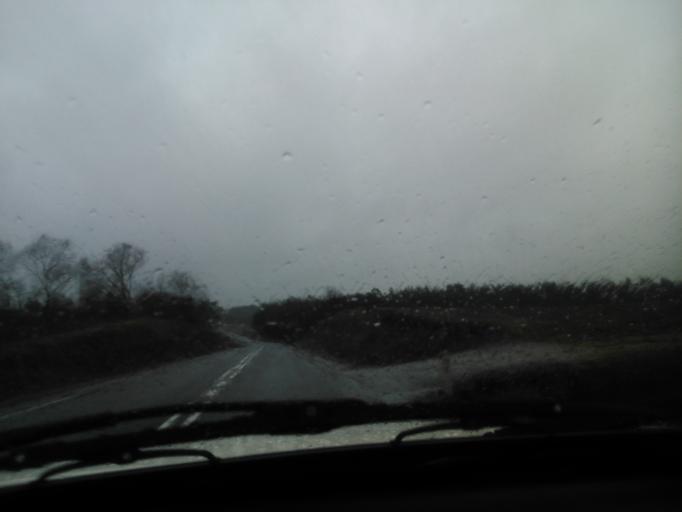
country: PL
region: Kujawsko-Pomorskie
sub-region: Powiat golubsko-dobrzynski
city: Radomin
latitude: 53.1011
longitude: 19.1349
